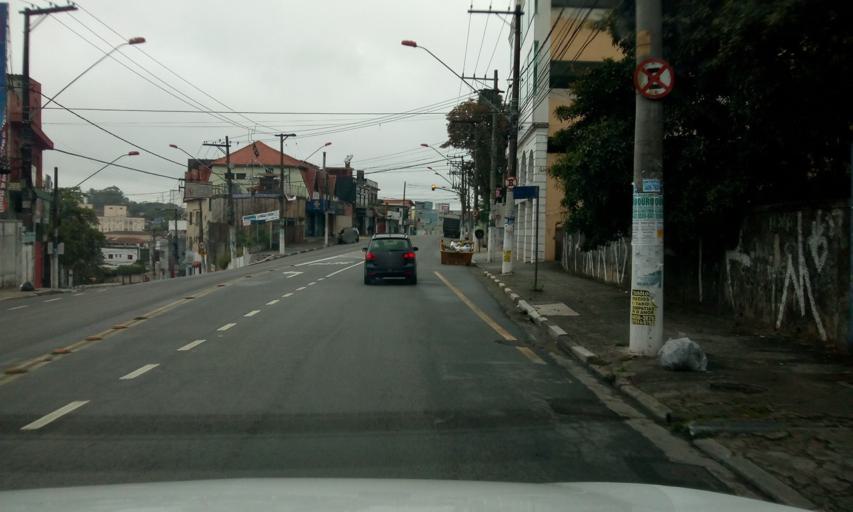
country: BR
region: Sao Paulo
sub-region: Diadema
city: Diadema
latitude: -23.6914
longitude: -46.6278
